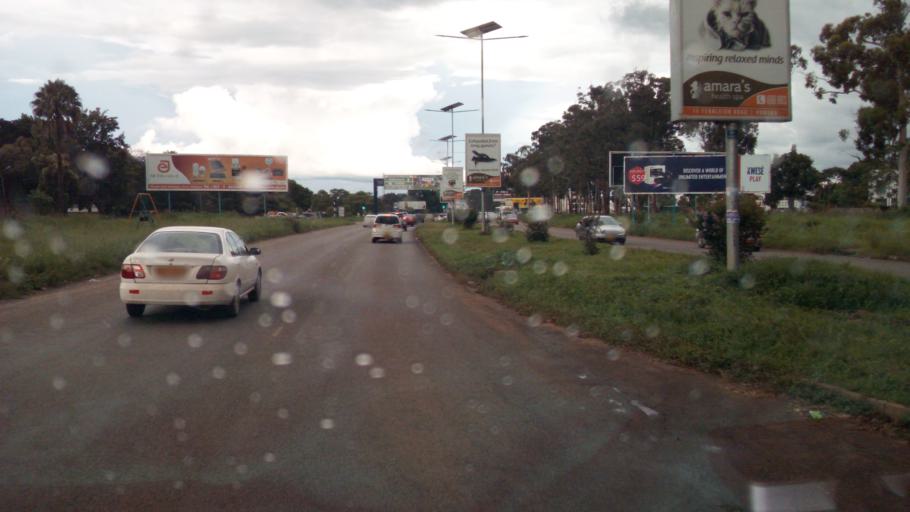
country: ZW
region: Harare
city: Harare
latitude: -17.7875
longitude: 31.0707
